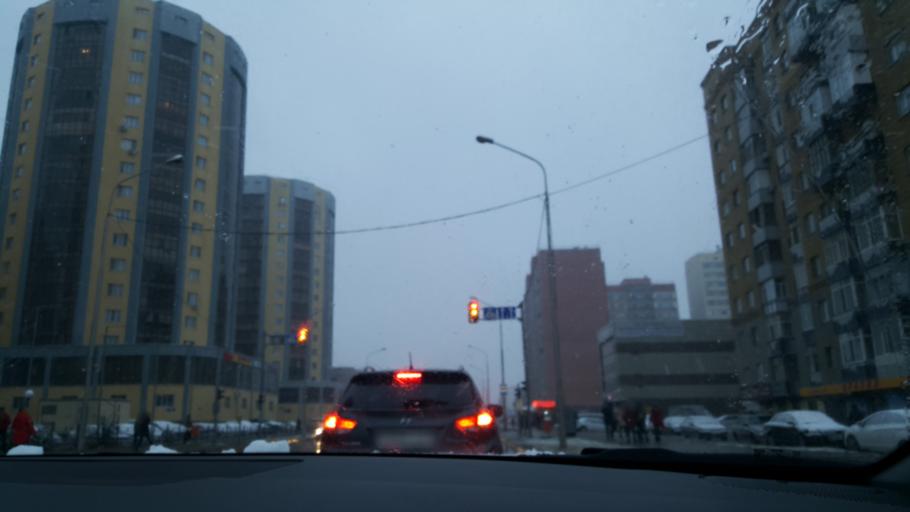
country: KZ
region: Astana Qalasy
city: Astana
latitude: 51.1580
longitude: 71.4948
